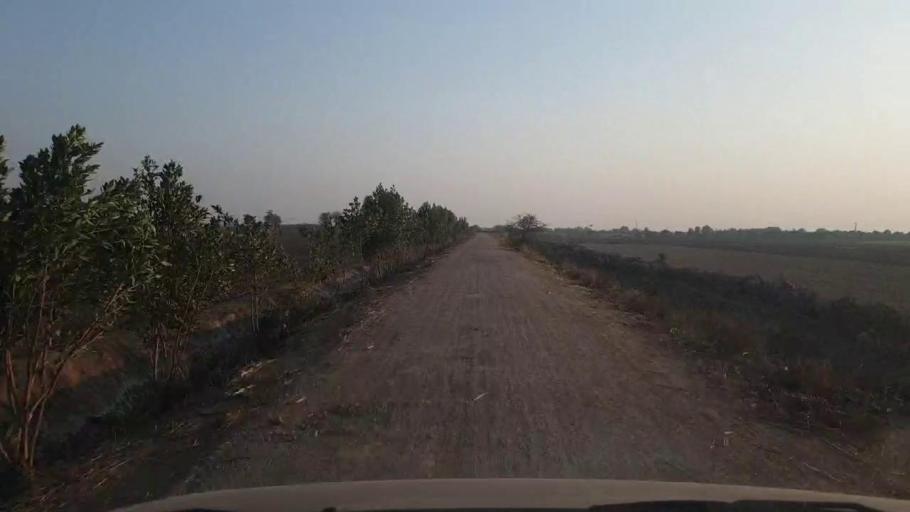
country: PK
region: Sindh
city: Mirwah Gorchani
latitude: 25.3492
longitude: 69.1533
